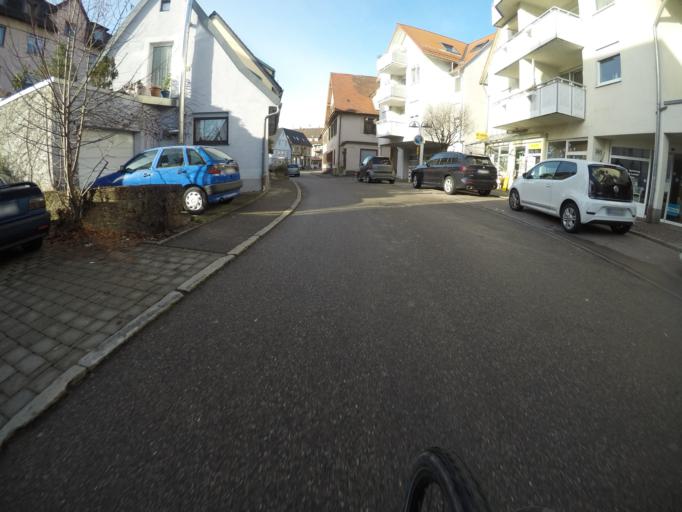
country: DE
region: Baden-Wuerttemberg
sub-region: Regierungsbezirk Stuttgart
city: Korb
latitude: 48.8430
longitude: 9.3605
